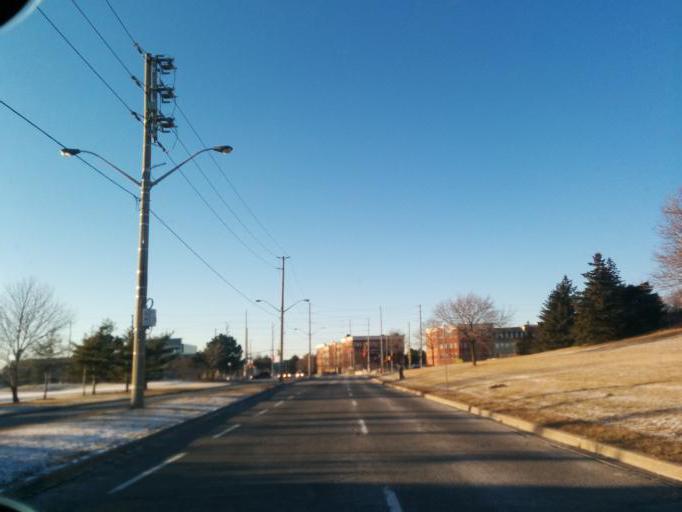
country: CA
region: Ontario
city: Etobicoke
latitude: 43.6550
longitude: -79.5970
